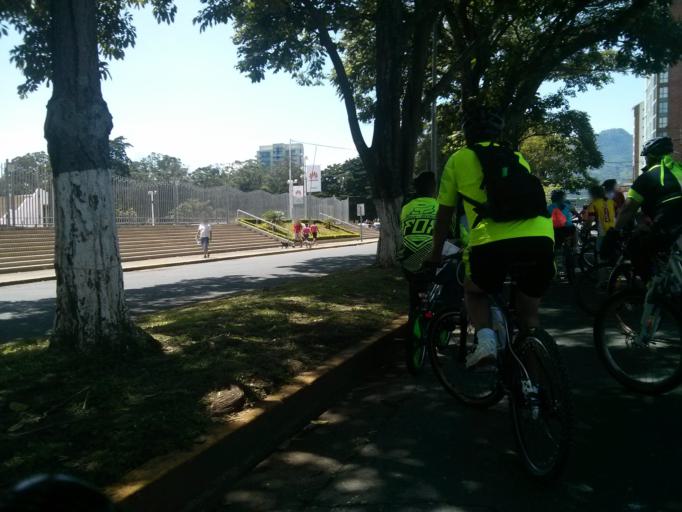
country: CR
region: San Jose
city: San Jose
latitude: 9.9369
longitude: -84.1095
